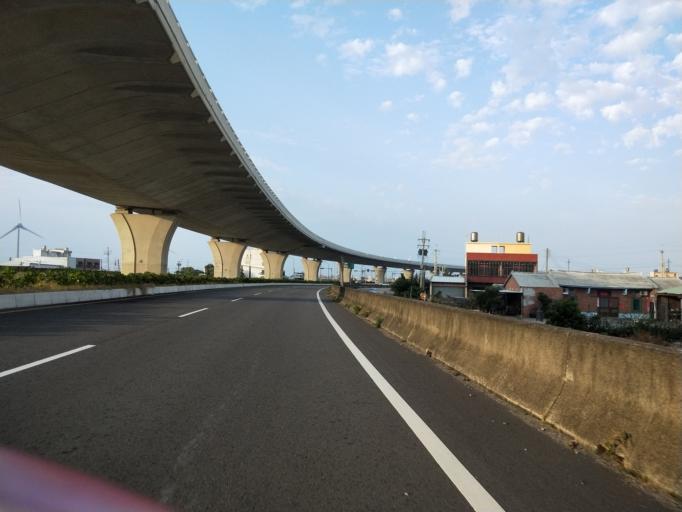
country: TW
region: Taiwan
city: Fengyuan
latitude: 24.4219
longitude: 120.6196
